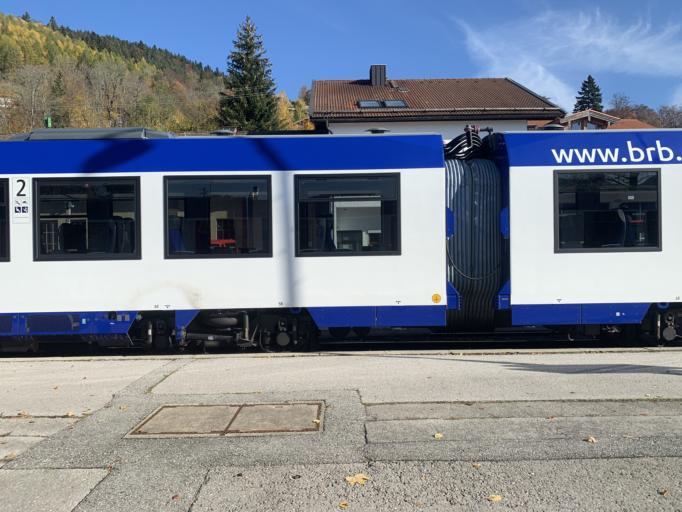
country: DE
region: Bavaria
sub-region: Upper Bavaria
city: Tegernsee
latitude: 47.7150
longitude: 11.7564
